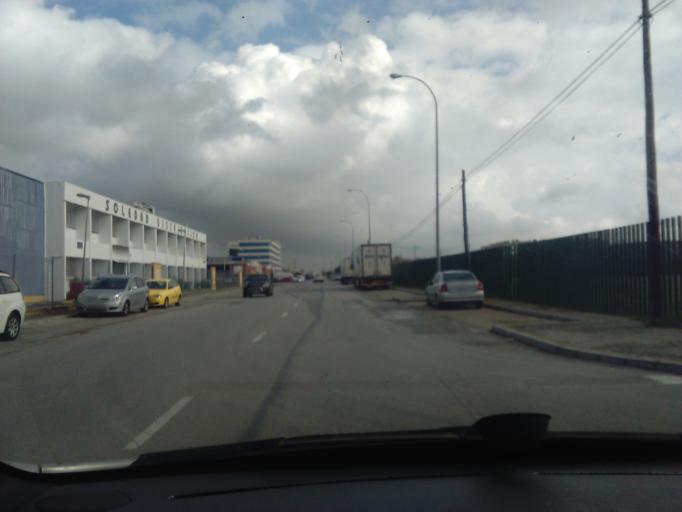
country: ES
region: Andalusia
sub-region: Provincia de Sevilla
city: Sevilla
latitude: 37.3817
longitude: -5.9226
